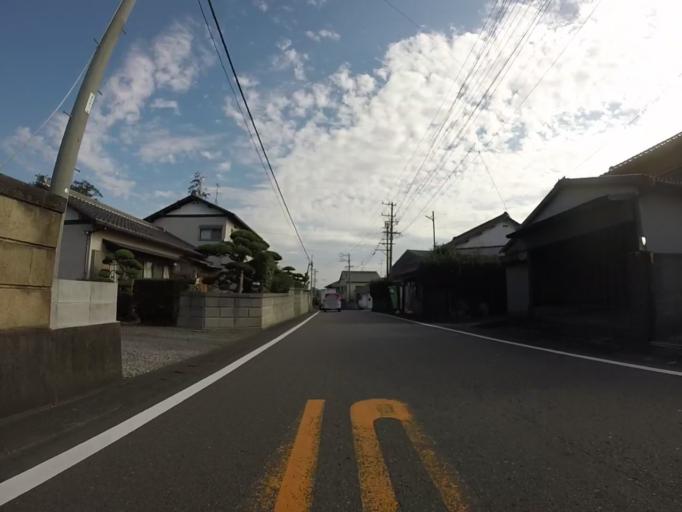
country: JP
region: Shizuoka
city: Shimada
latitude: 34.7796
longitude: 138.2331
